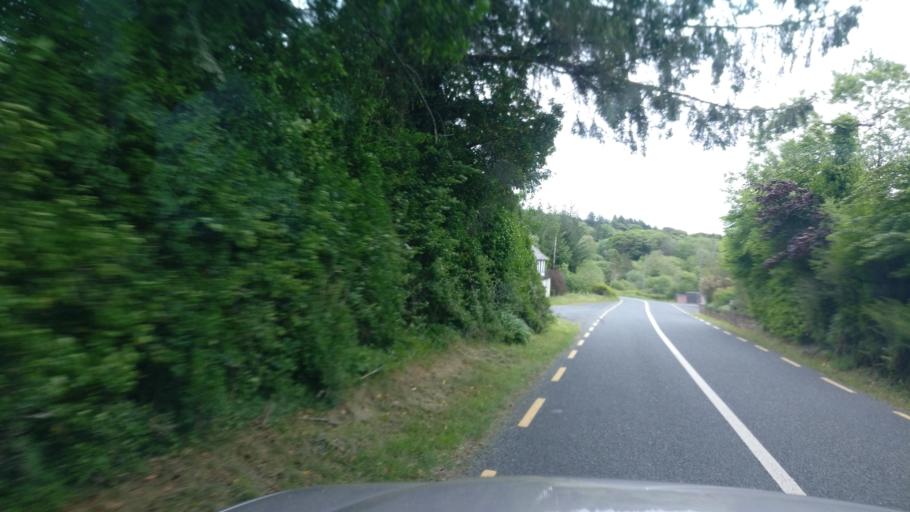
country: IE
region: Connaught
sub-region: County Galway
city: Loughrea
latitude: 53.0642
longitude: -8.6190
